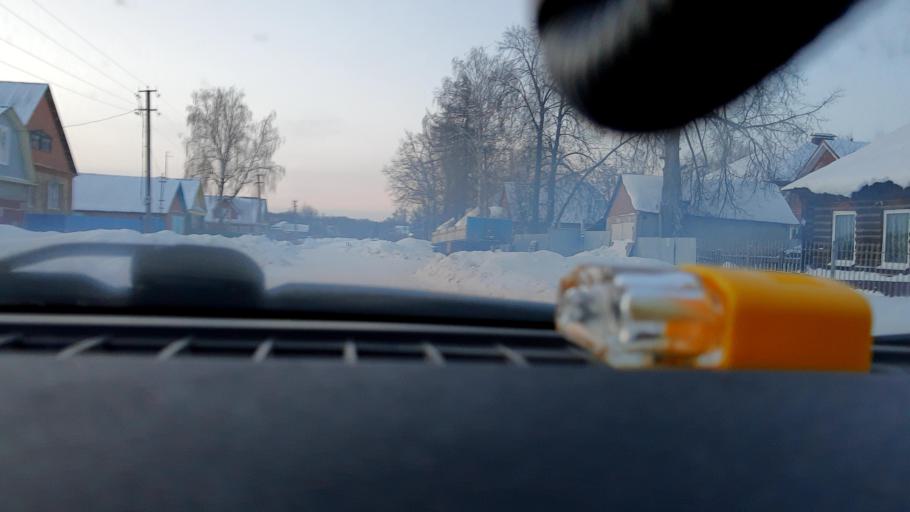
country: RU
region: Bashkortostan
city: Iglino
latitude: 54.7334
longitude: 56.3253
